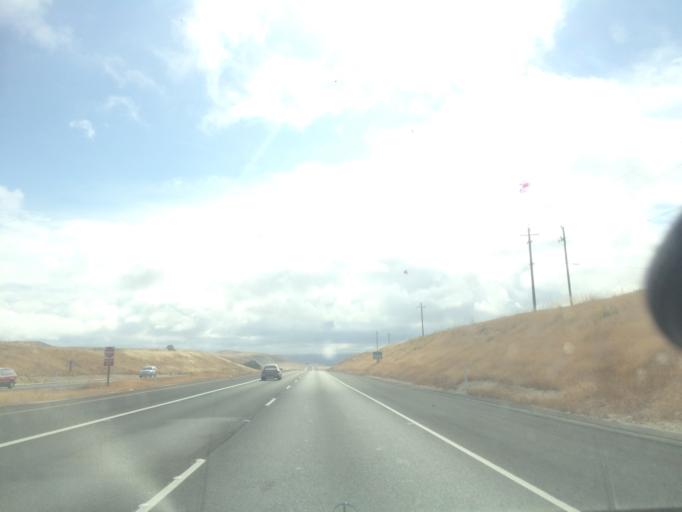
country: US
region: California
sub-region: San Luis Obispo County
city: Shandon
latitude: 35.6589
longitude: -120.4803
